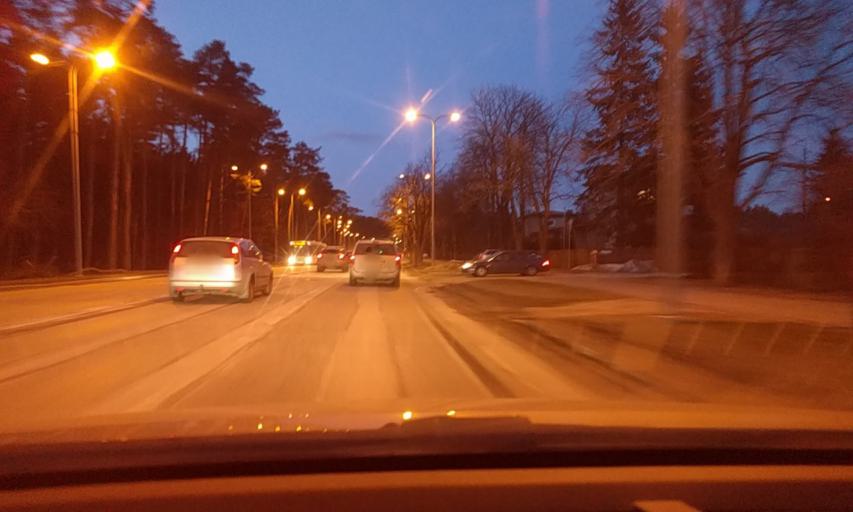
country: EE
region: Harju
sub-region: Viimsi vald
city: Viimsi
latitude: 59.4718
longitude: 24.8360
